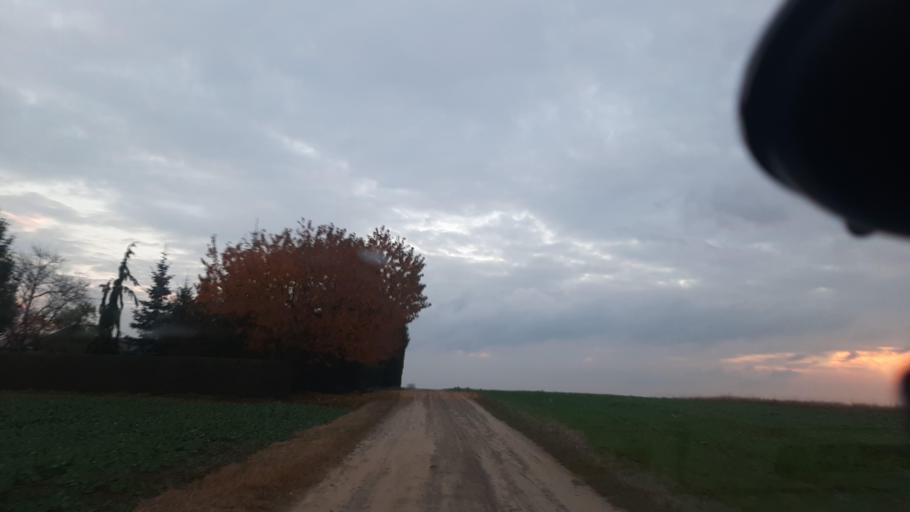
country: PL
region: Lublin Voivodeship
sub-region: Powiat lubelski
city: Jastkow
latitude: 51.3310
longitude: 22.3922
